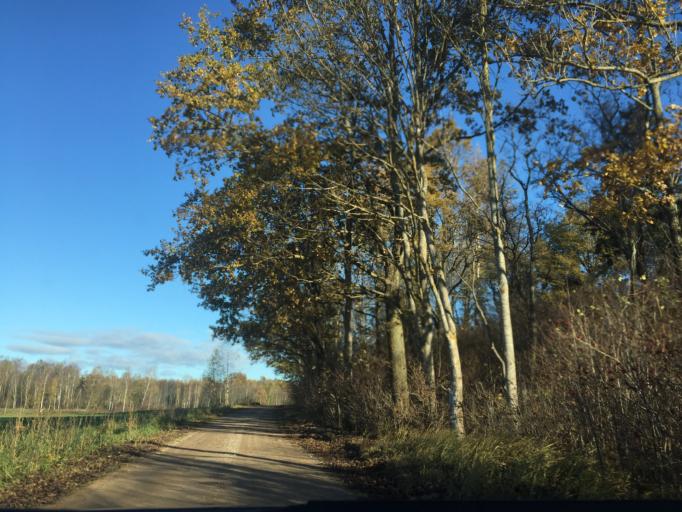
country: LV
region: Engure
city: Smarde
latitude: 56.9225
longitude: 23.2857
